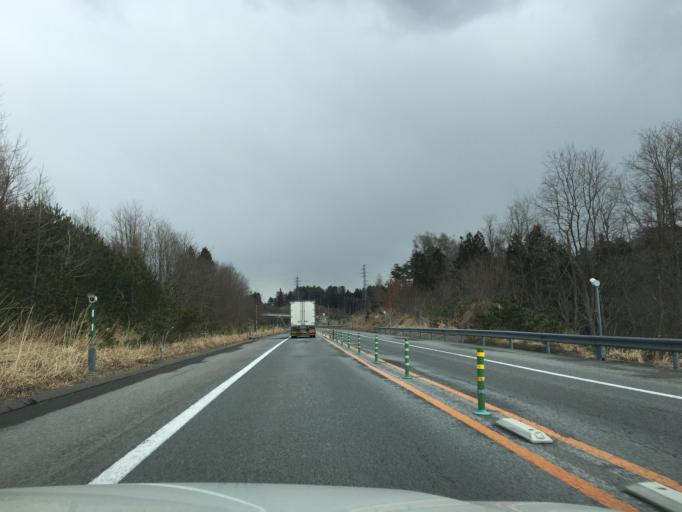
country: JP
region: Aomori
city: Aomori Shi
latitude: 40.8012
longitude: 140.6976
